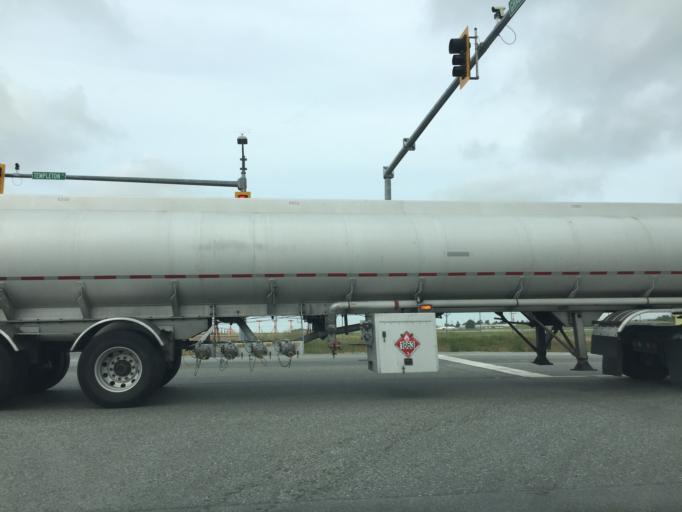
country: CA
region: British Columbia
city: Richmond
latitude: 49.1994
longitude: -123.1489
